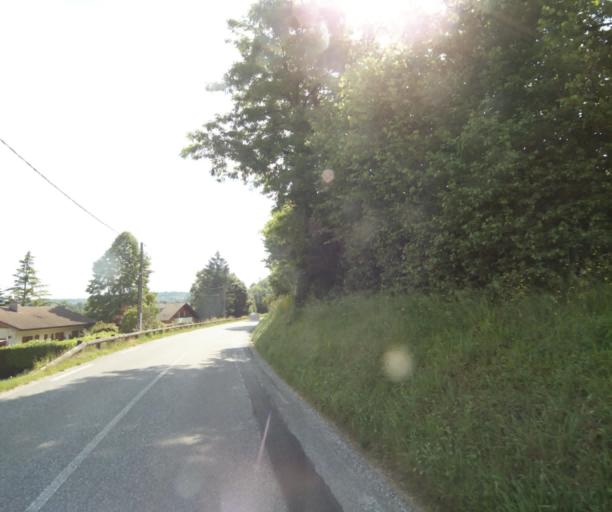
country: FR
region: Rhone-Alpes
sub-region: Departement de la Haute-Savoie
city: Allinges
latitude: 46.3362
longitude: 6.4708
